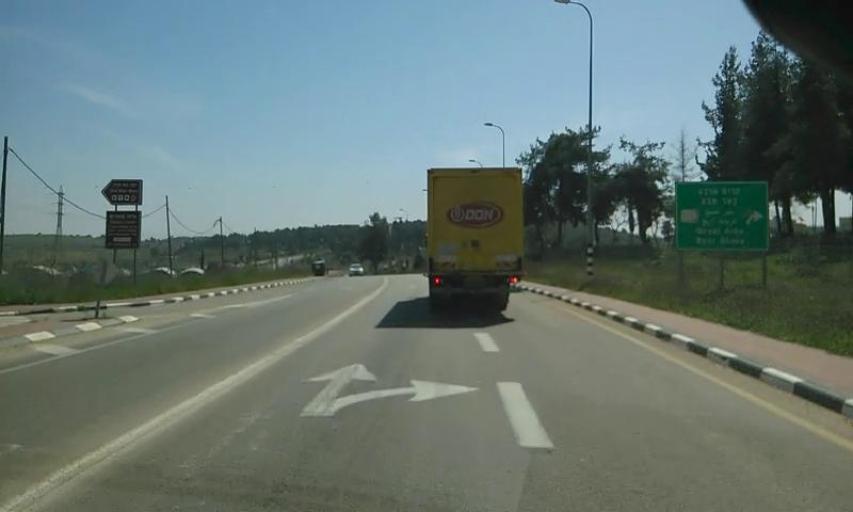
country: PS
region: West Bank
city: Shuyukh al `Arrub
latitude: 31.6473
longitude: 35.1302
